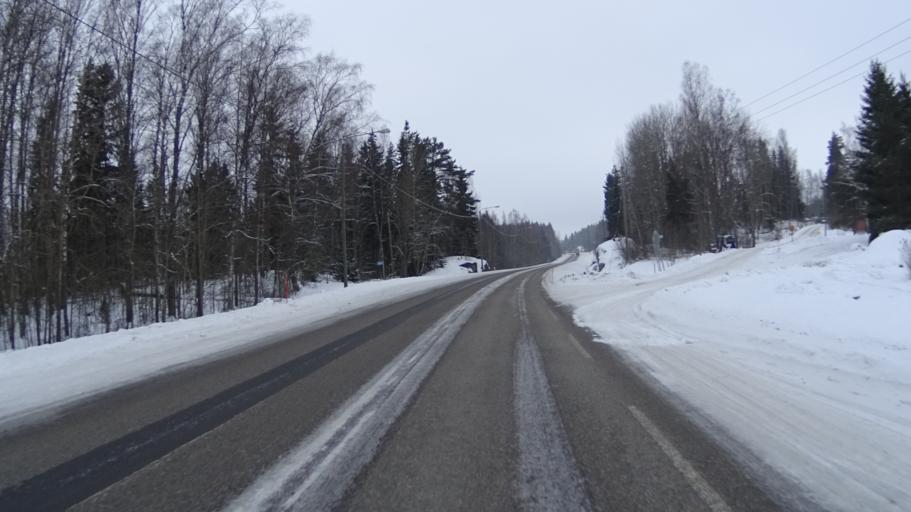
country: FI
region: Uusimaa
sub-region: Helsinki
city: Vihti
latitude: 60.3550
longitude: 24.1808
